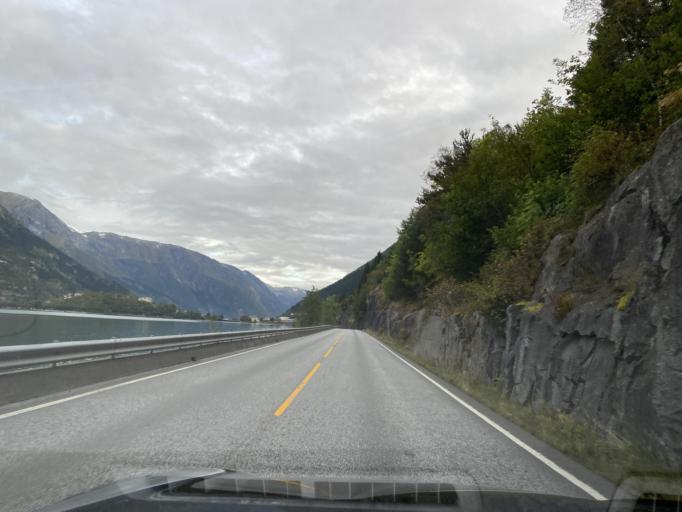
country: NO
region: Hordaland
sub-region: Odda
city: Odda
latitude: 60.0400
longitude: 6.5618
